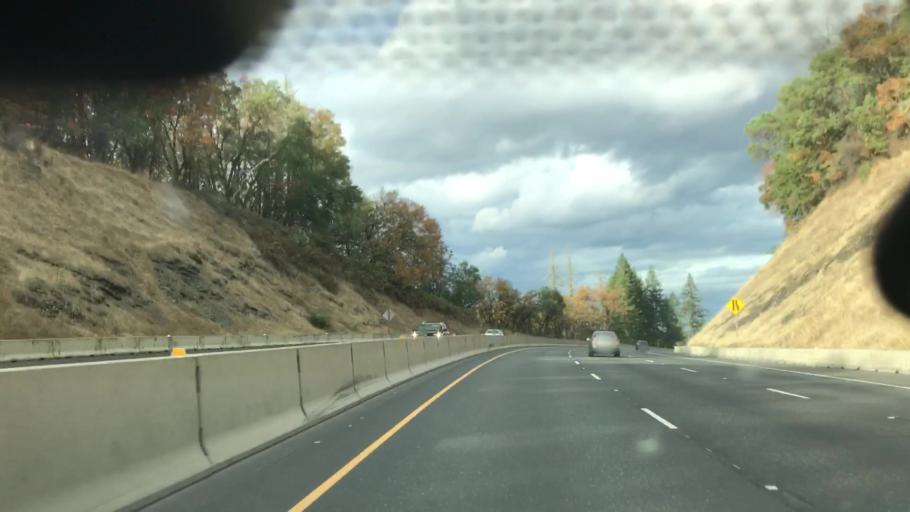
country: US
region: Oregon
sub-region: Douglas County
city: Sutherlin
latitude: 43.4017
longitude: -123.3358
